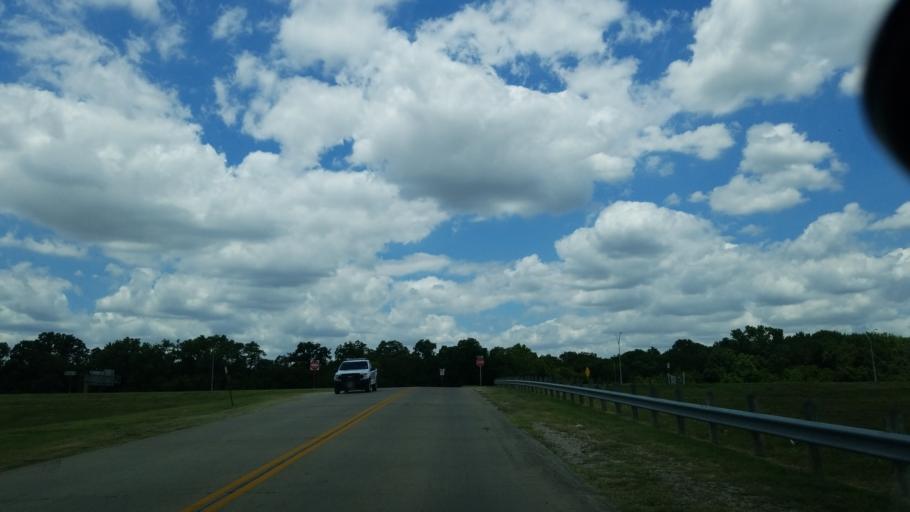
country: US
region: Texas
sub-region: Dallas County
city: Dallas
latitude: 32.7459
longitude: -96.7456
